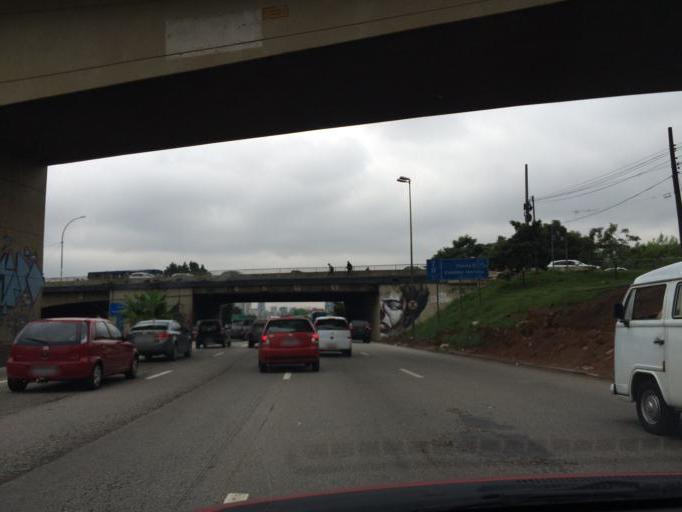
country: BR
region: Sao Paulo
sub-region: Sao Paulo
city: Sao Paulo
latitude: -23.5717
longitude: -46.7022
